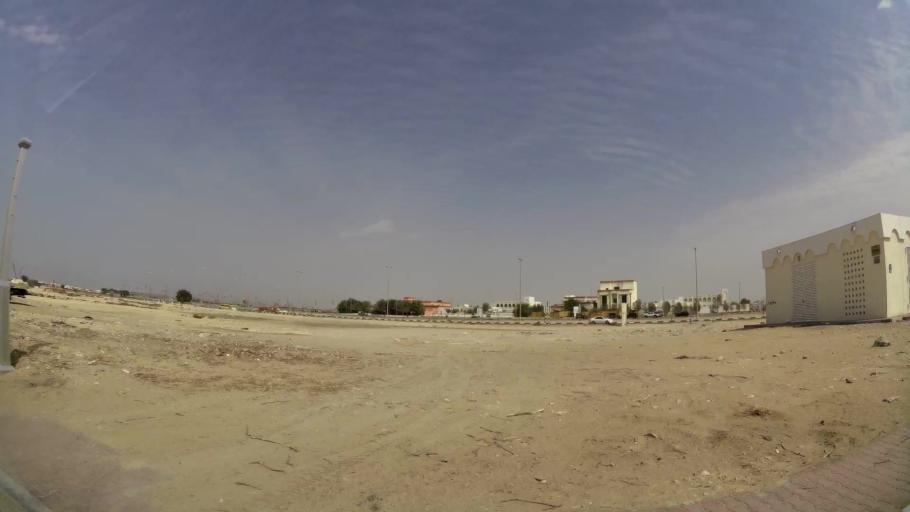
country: AE
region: Abu Dhabi
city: Abu Dhabi
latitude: 24.5588
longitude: 54.6848
